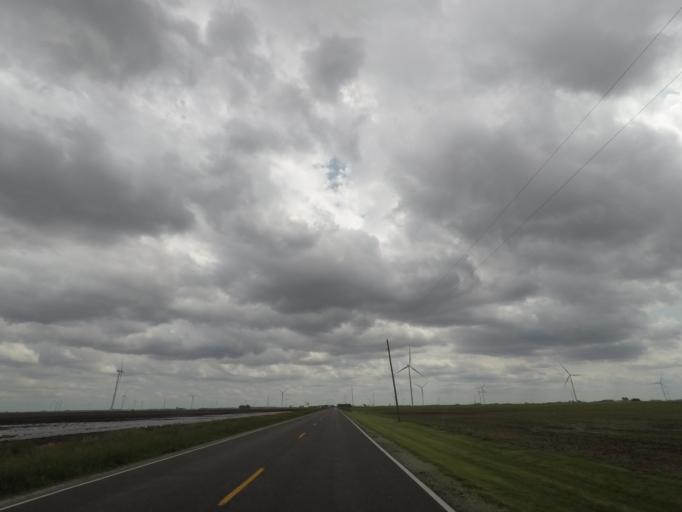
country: US
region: Illinois
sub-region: Macon County
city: Warrensburg
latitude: 40.0194
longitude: -89.0856
